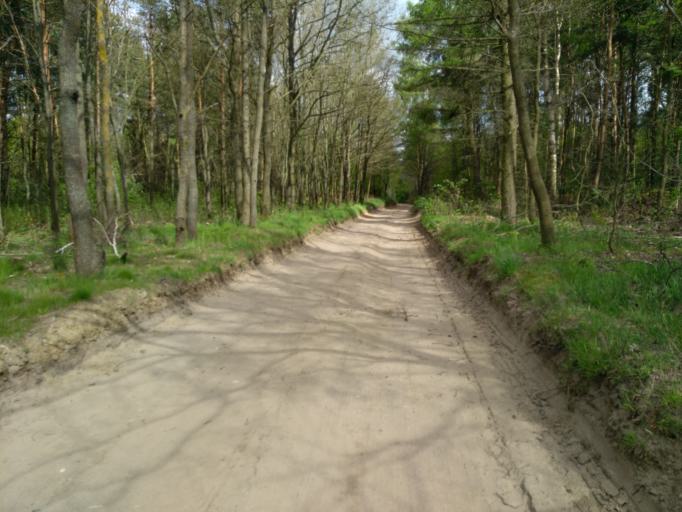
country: PL
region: Pomeranian Voivodeship
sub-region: Powiat kartuski
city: Banino
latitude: 54.4123
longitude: 18.4082
